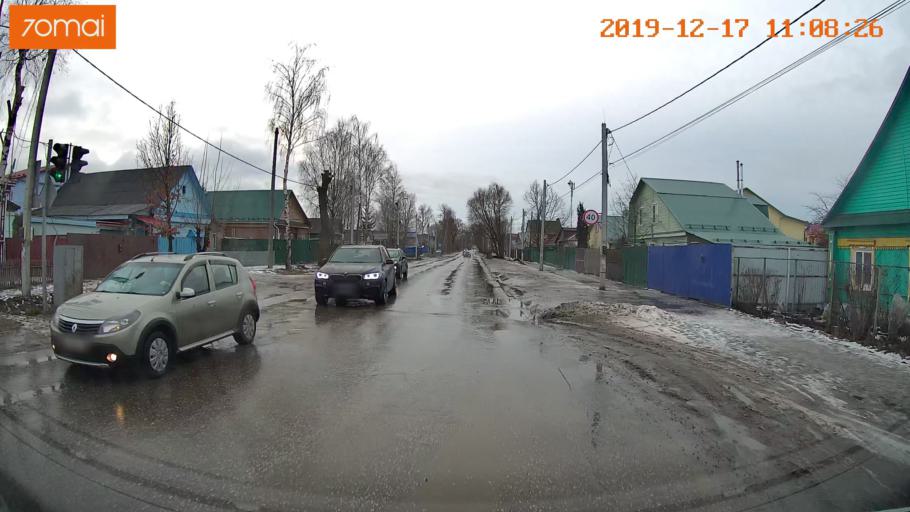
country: RU
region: Vladimir
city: Gus'-Khrustal'nyy
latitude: 55.6076
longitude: 40.6433
